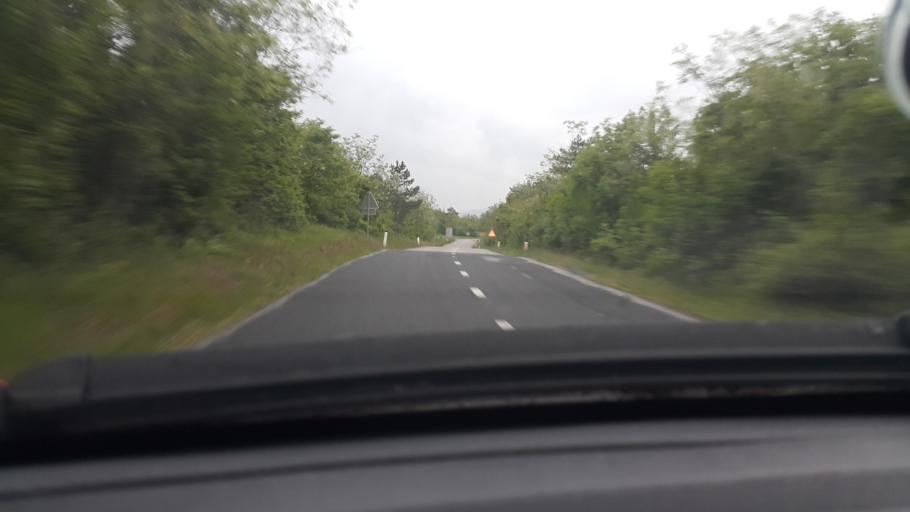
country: SI
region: Sezana
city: Sezana
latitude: 45.7775
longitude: 13.8682
